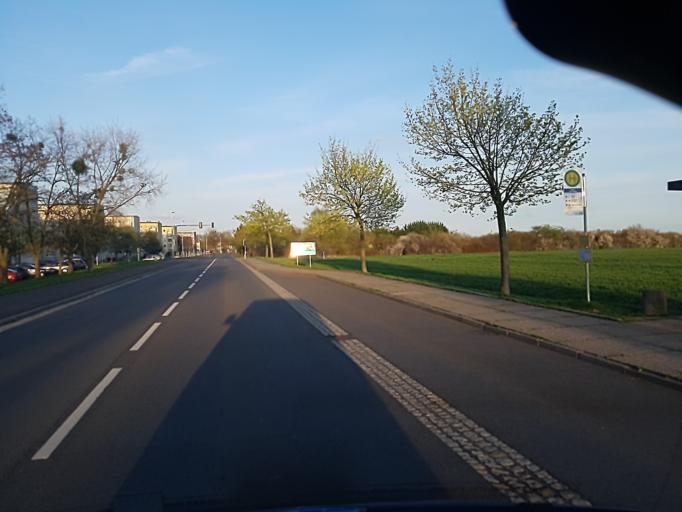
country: DE
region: Saxony
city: Zinna
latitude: 51.5654
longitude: 12.9665
